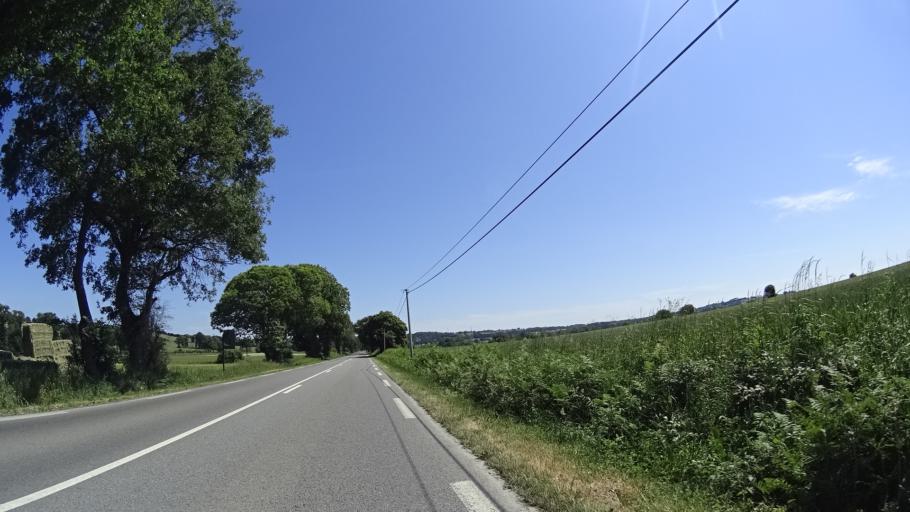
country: FR
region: Brittany
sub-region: Departement d'Ille-et-Vilaine
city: Bain-de-Bretagne
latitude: 47.8377
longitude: -1.7303
